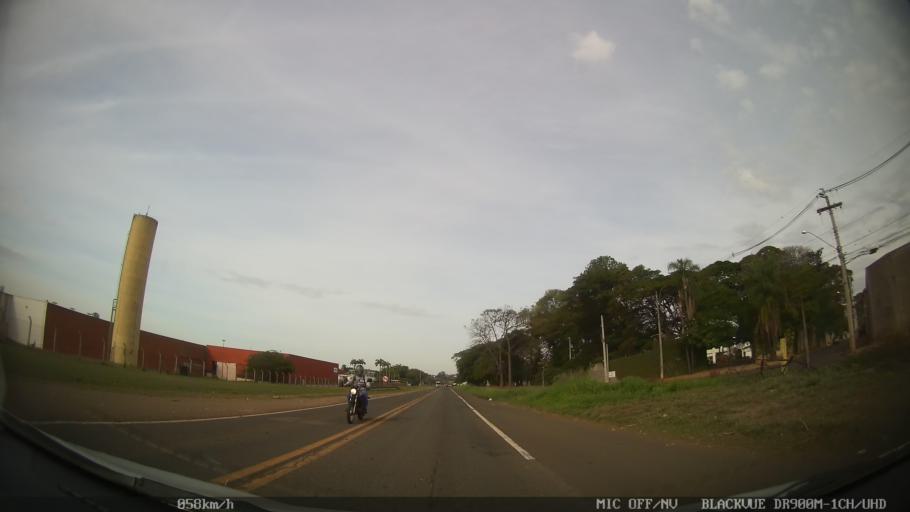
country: BR
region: Sao Paulo
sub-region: Piracicaba
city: Piracicaba
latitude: -22.7380
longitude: -47.5938
